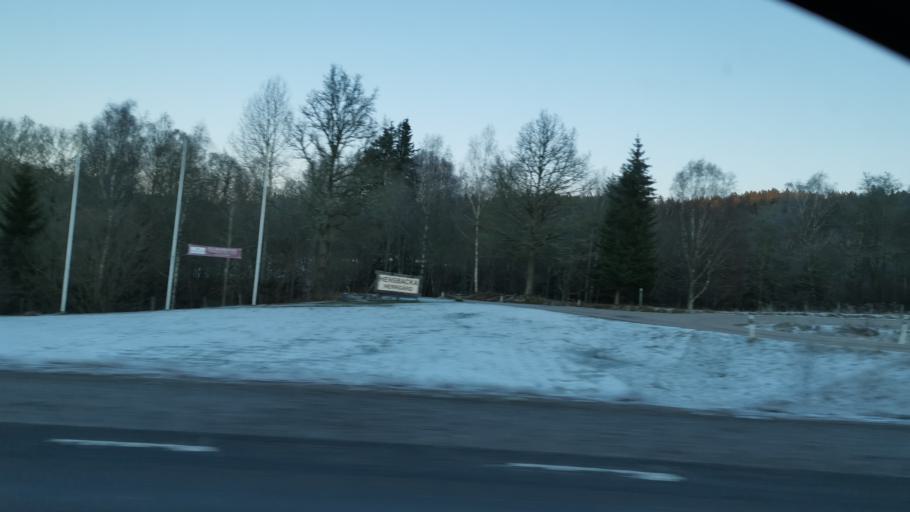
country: SE
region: Vaestra Goetaland
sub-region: Munkedals Kommun
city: Munkedal
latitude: 58.4310
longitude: 11.7202
